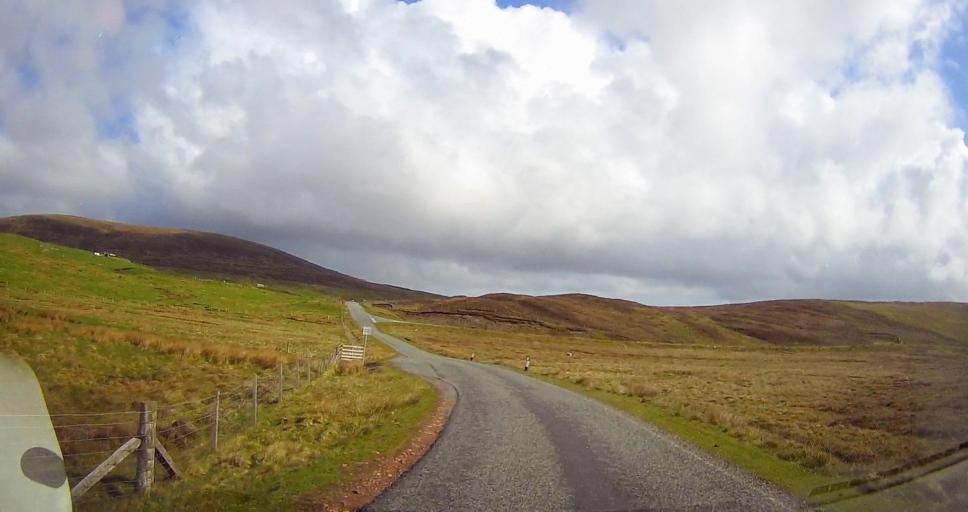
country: GB
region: Scotland
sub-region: Shetland Islands
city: Lerwick
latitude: 60.5166
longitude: -1.3781
